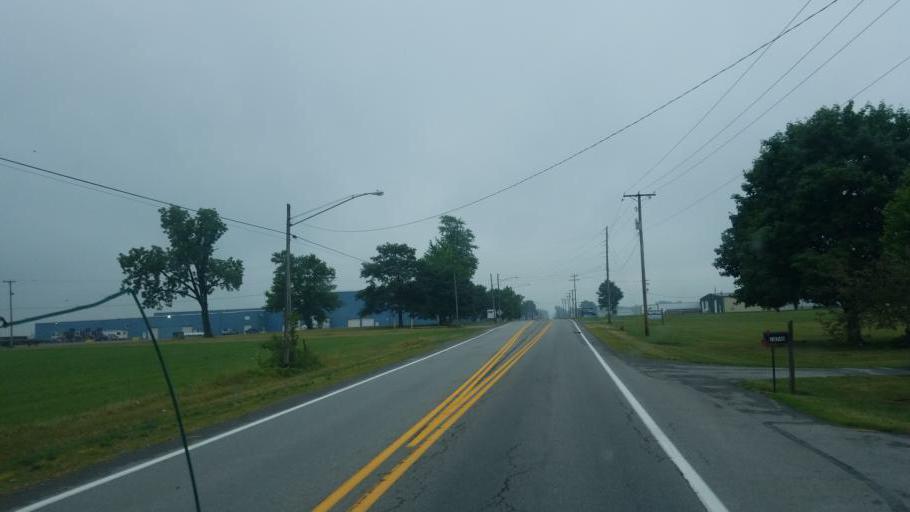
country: US
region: Ohio
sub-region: Defiance County
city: Hicksville
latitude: 41.2851
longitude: -84.7783
